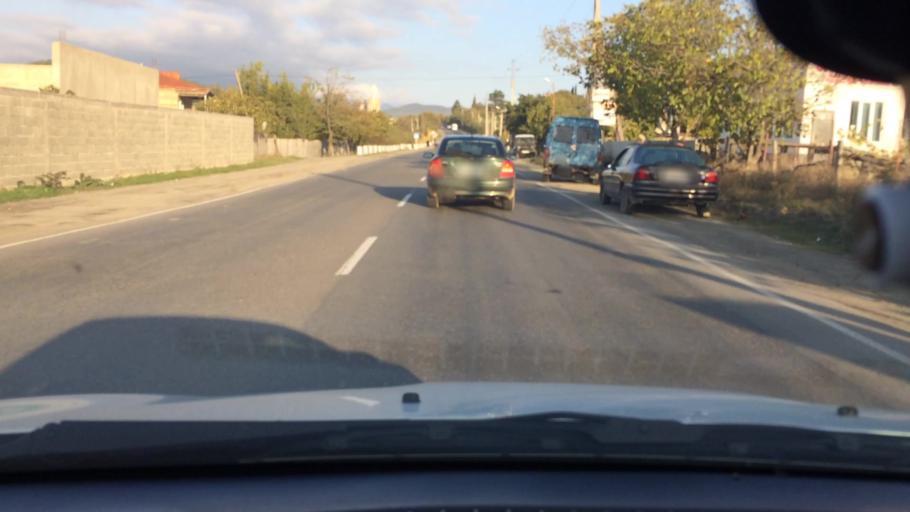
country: GE
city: Surami
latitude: 42.0150
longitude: 43.5728
